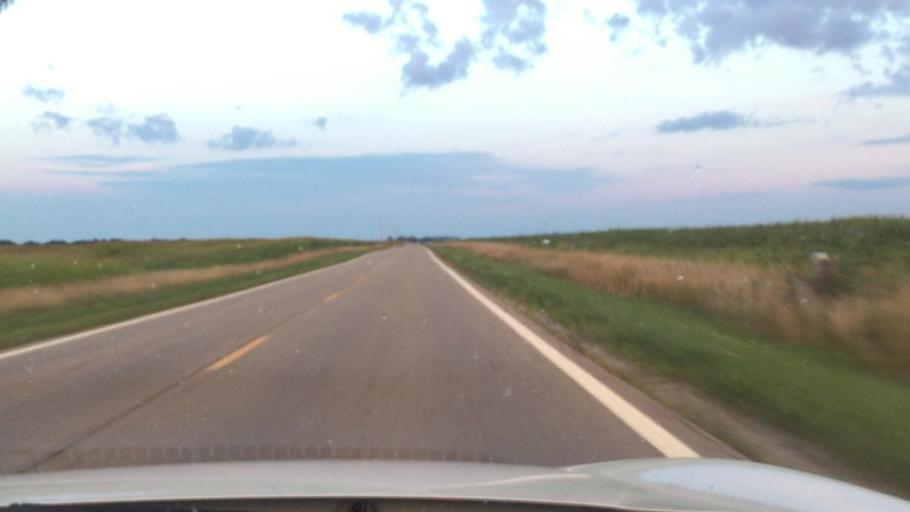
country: US
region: Ohio
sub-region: Madison County
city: Choctaw Lake
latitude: 40.0162
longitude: -83.4635
